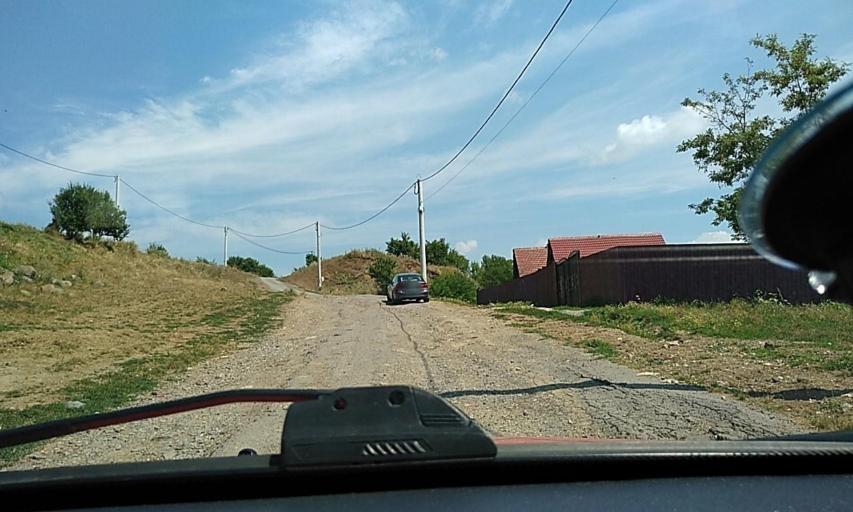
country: RO
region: Brasov
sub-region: Comuna Hoghiz
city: Hoghiz
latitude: 46.0266
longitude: 25.4140
